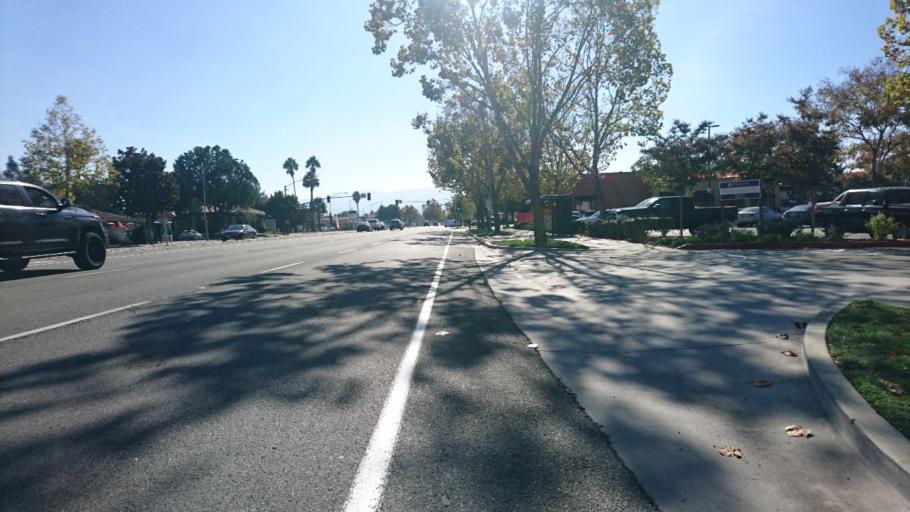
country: US
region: California
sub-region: Santa Clara County
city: Campbell
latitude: 37.2882
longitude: -121.9318
